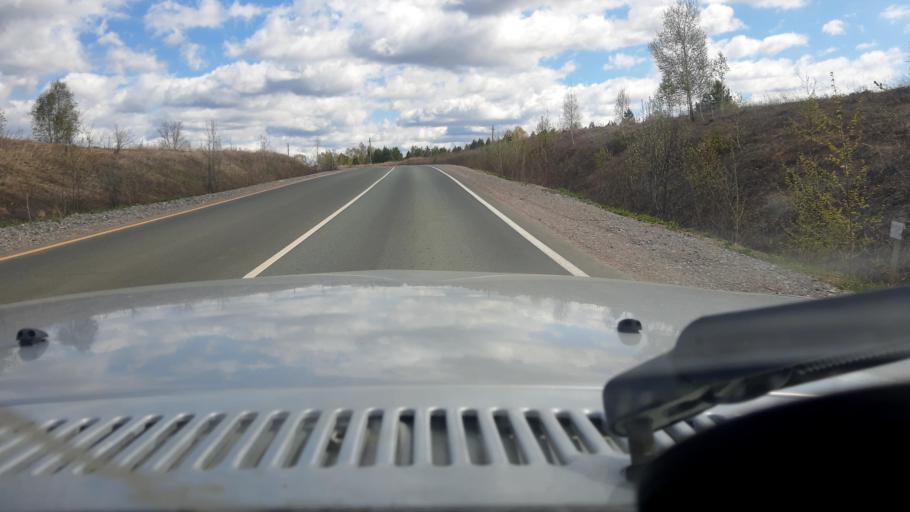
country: RU
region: Bashkortostan
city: Pavlovka
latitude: 55.3551
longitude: 56.4001
